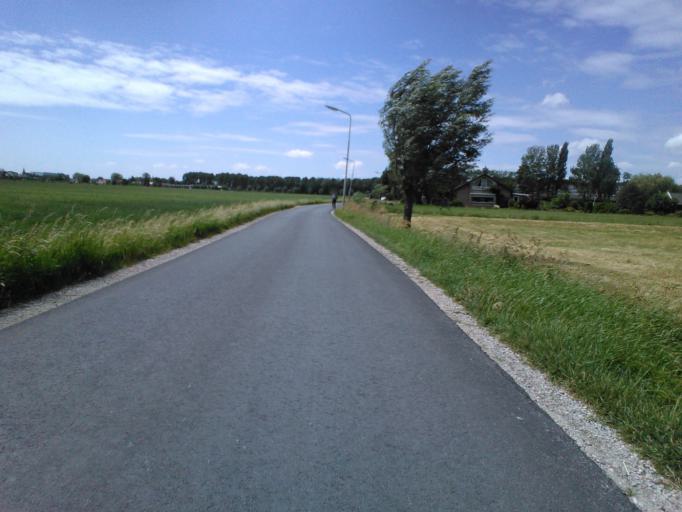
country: NL
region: South Holland
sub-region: Molenwaard
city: Nieuw-Lekkerland
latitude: 51.8674
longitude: 4.6845
